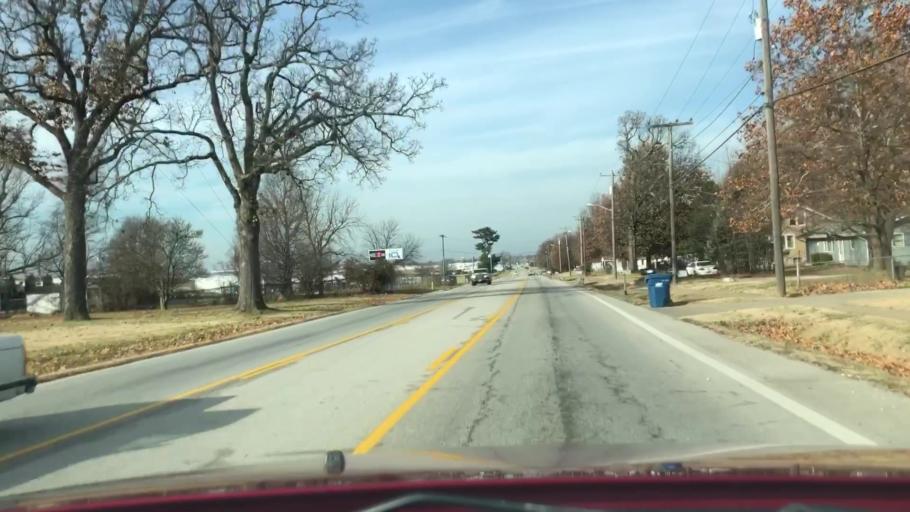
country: US
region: Missouri
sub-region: Greene County
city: Springfield
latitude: 37.2248
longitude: -93.2404
